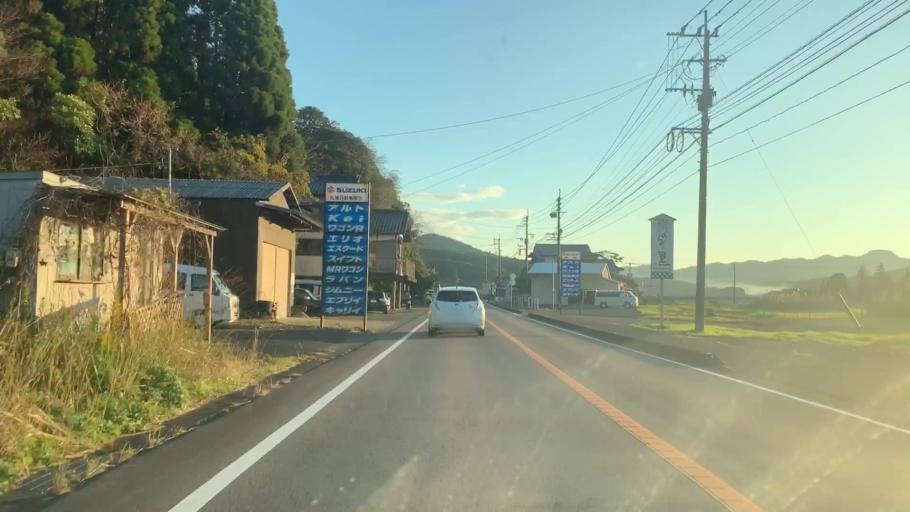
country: JP
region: Saga Prefecture
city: Imaricho-ko
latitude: 33.2698
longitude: 129.9646
